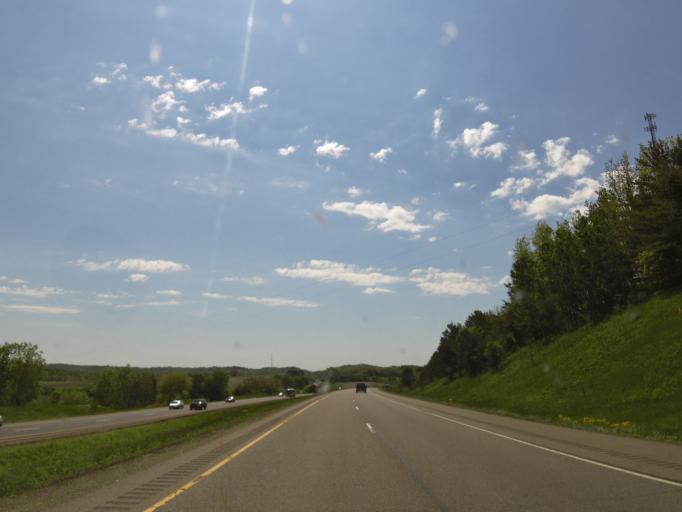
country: US
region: Wisconsin
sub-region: Trempealeau County
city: Osseo
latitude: 44.5031
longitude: -91.1289
